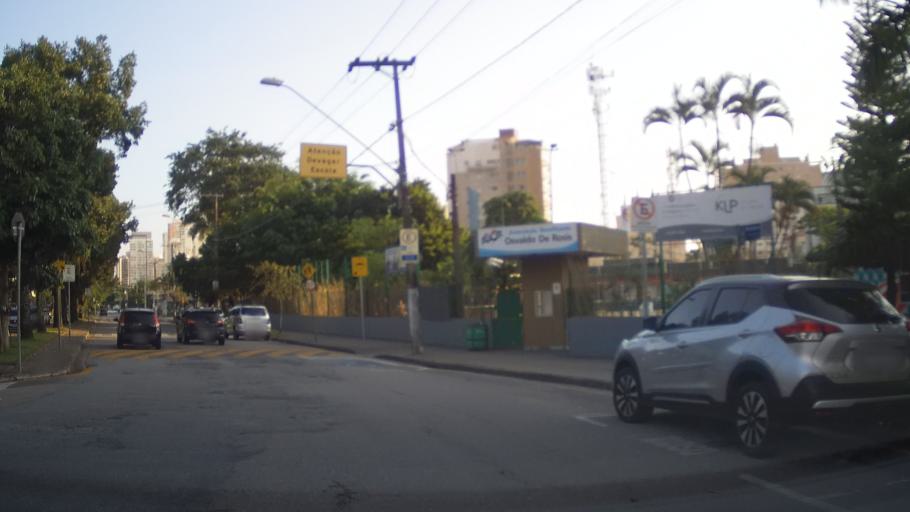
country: BR
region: Sao Paulo
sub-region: Santos
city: Santos
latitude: -23.9776
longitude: -46.3002
